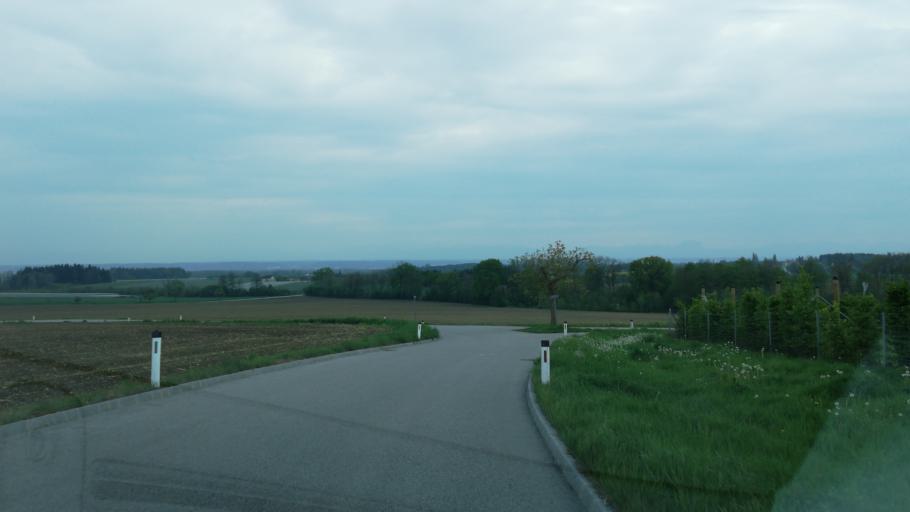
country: AT
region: Upper Austria
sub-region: Wels-Land
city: Buchkirchen
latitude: 48.2356
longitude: 14.0555
